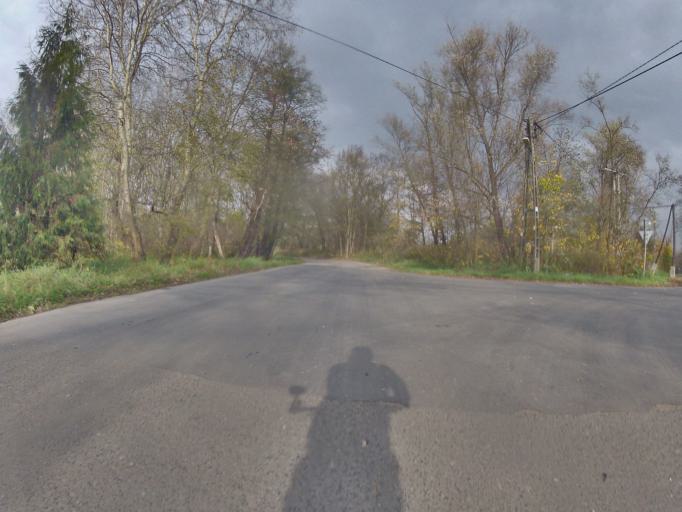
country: PL
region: Lesser Poland Voivodeship
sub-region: Powiat wielicki
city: Wegrzce Wielkie
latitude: 50.0583
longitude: 20.1020
